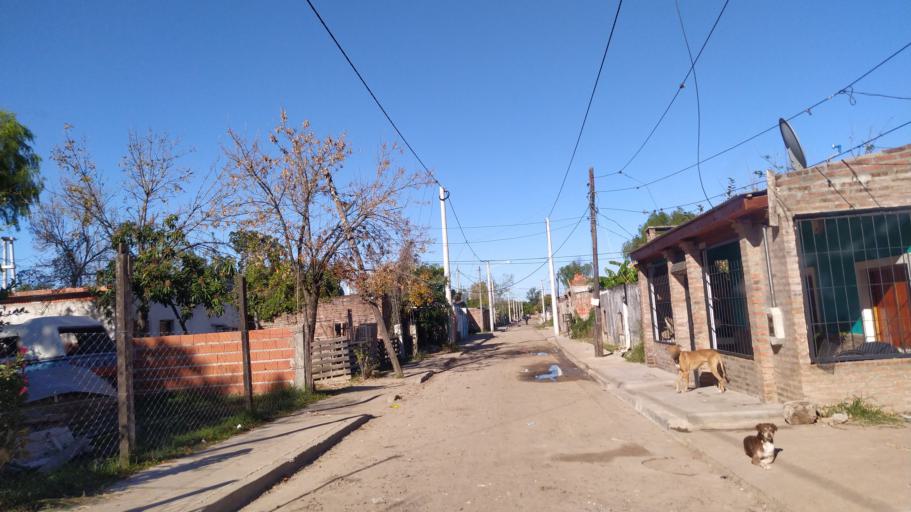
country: AR
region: Corrientes
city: Corrientes
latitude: -27.4945
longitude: -58.8061
